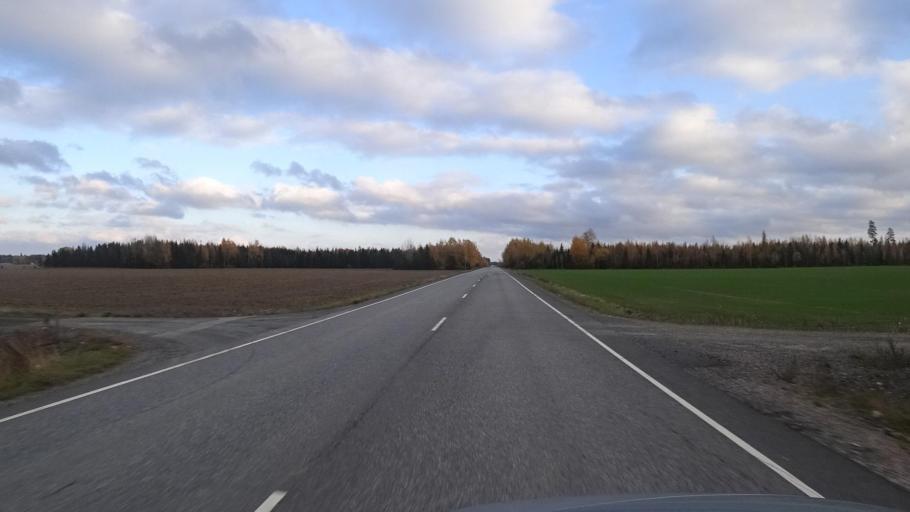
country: FI
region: Varsinais-Suomi
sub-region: Loimaa
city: Alastaro
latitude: 60.9070
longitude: 22.9231
